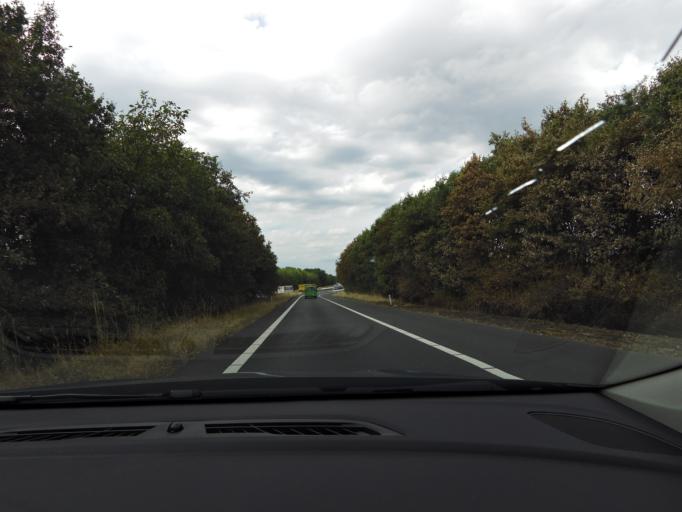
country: NL
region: North Brabant
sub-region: Gemeente Cuijk
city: Cuijk
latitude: 51.7716
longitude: 5.8381
